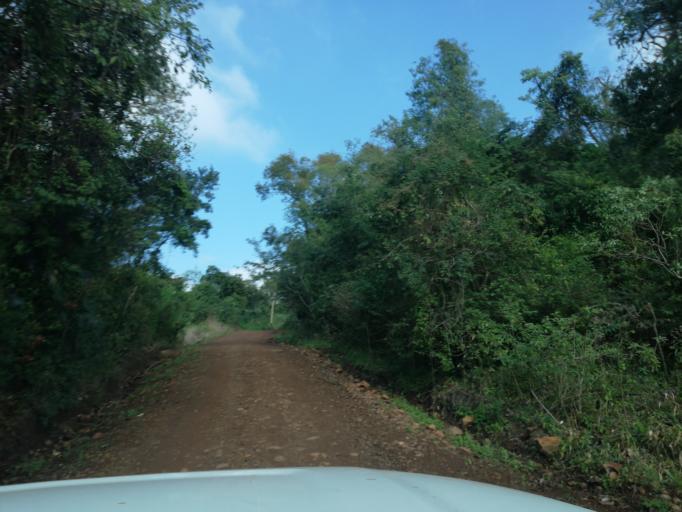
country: AR
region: Misiones
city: Cerro Azul
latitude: -27.5744
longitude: -55.5039
